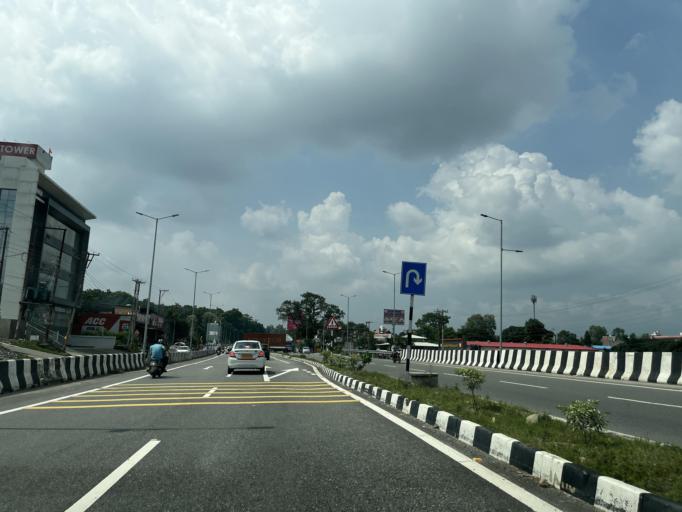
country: IN
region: Uttarakhand
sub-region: Dehradun
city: Raipur
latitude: 30.2456
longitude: 78.0982
